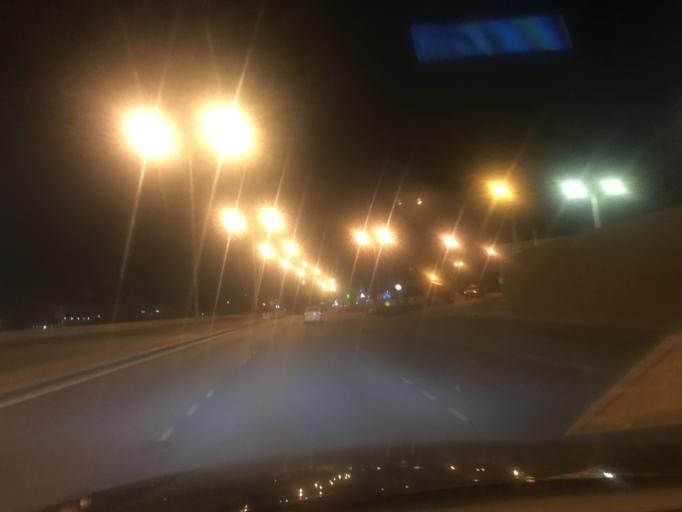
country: SA
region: Ar Riyad
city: Riyadh
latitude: 24.6932
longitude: 46.6108
